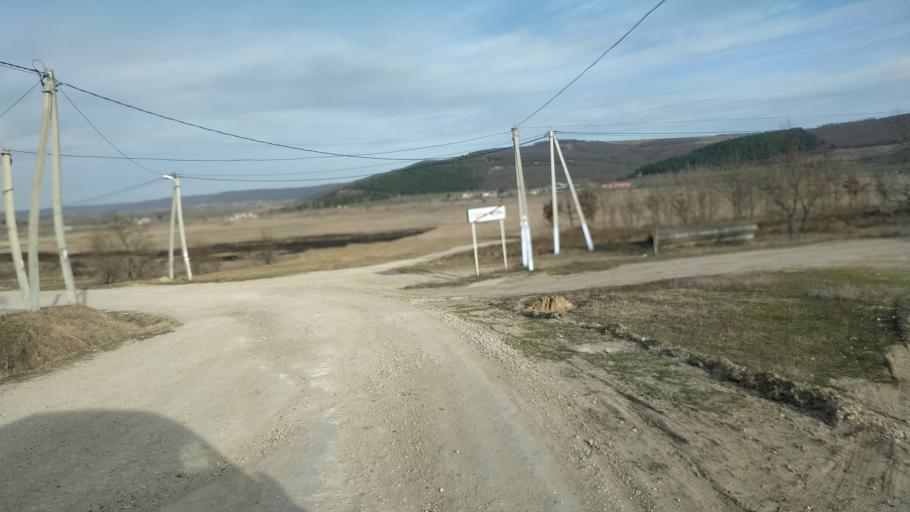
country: RO
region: Vaslui
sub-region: Comuna Dranceni
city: Dranceni
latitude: 46.8435
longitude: 28.1879
